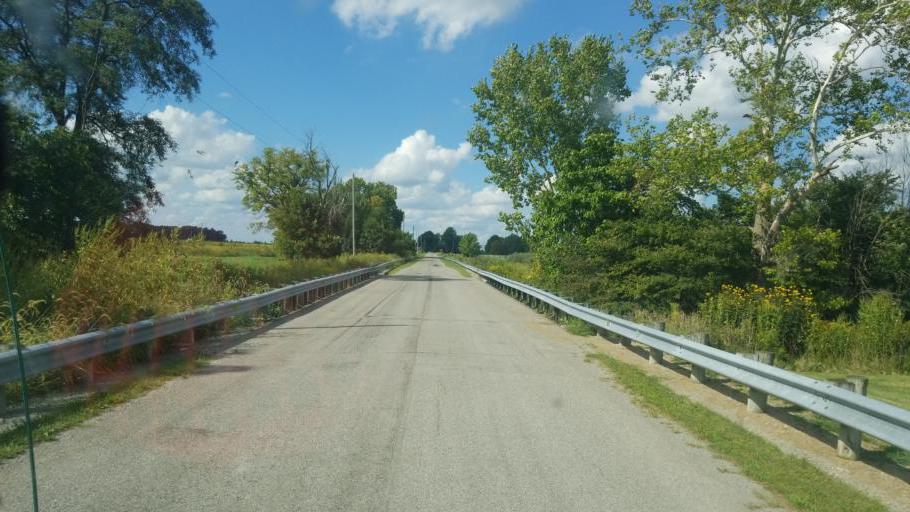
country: US
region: Ohio
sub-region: Union County
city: Richwood
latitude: 40.4766
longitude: -83.3286
